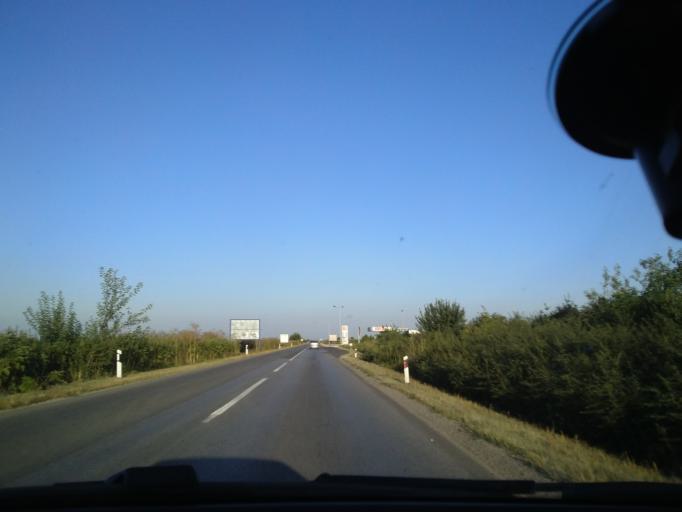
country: RS
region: Autonomna Pokrajina Vojvodina
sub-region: Juznobacki Okrug
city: Backi Petrovac
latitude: 45.3469
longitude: 19.6277
